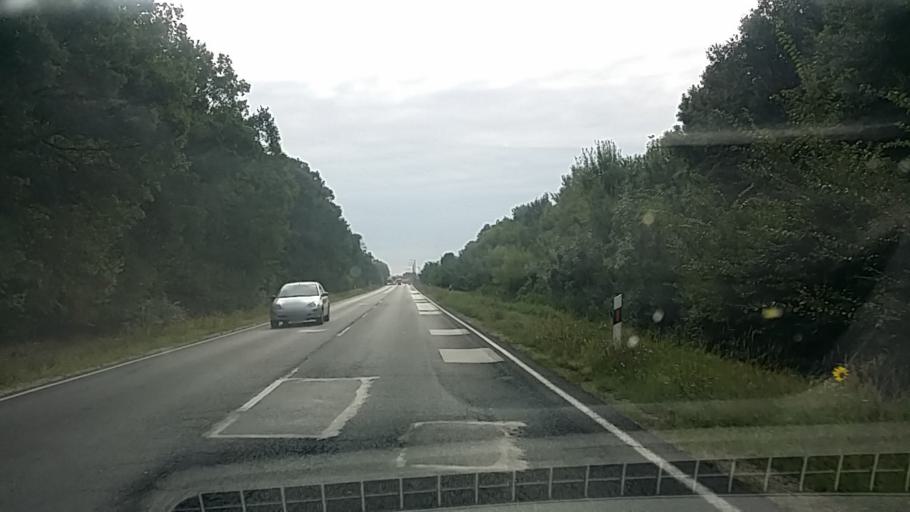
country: HU
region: Gyor-Moson-Sopron
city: Kapuvar
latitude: 47.5879
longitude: 16.9687
